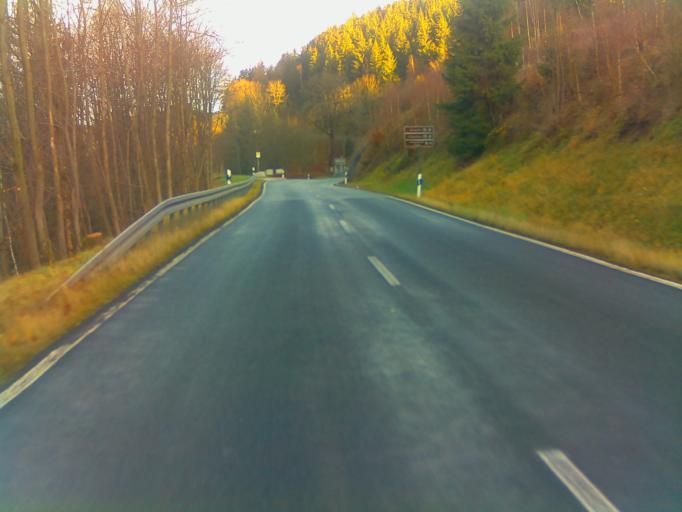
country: DE
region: Thuringia
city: Meuselbach
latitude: 50.5718
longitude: 11.0723
